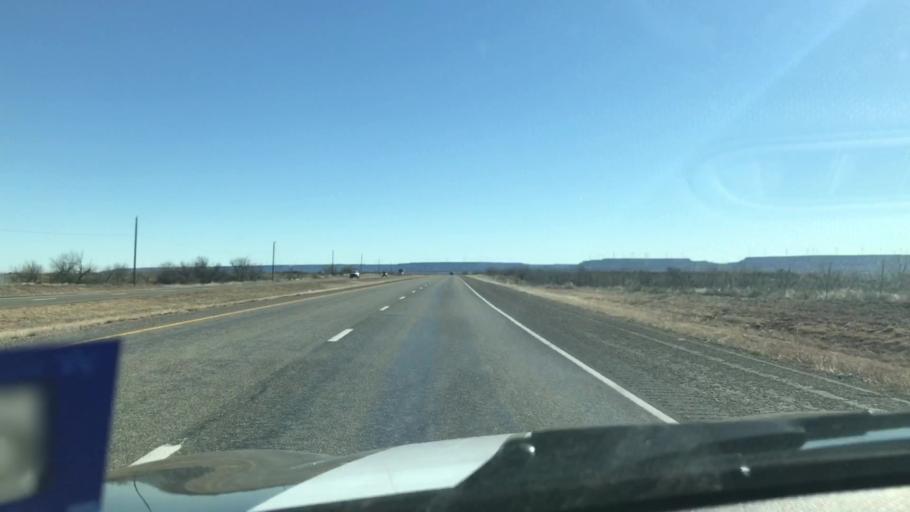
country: US
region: Texas
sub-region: Garza County
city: Post
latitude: 33.0875
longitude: -101.2434
